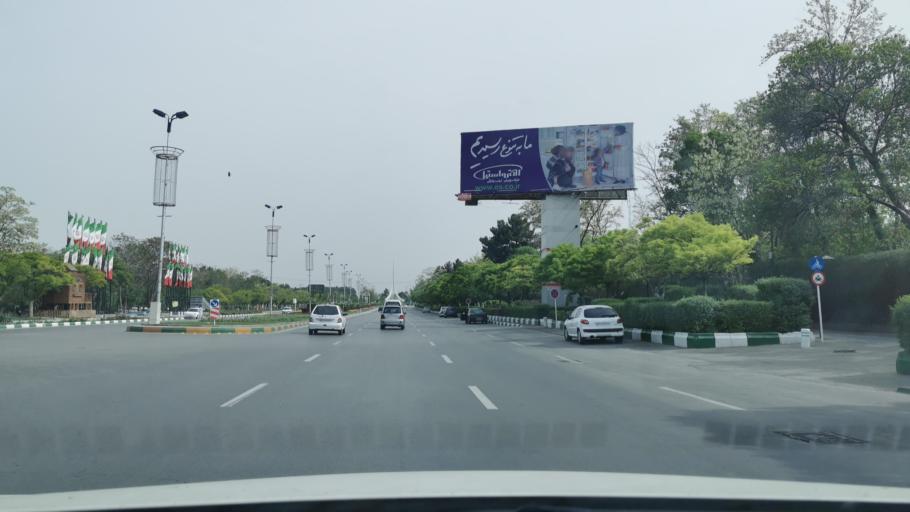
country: IR
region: Razavi Khorasan
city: Mashhad
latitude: 36.2470
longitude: 59.6196
